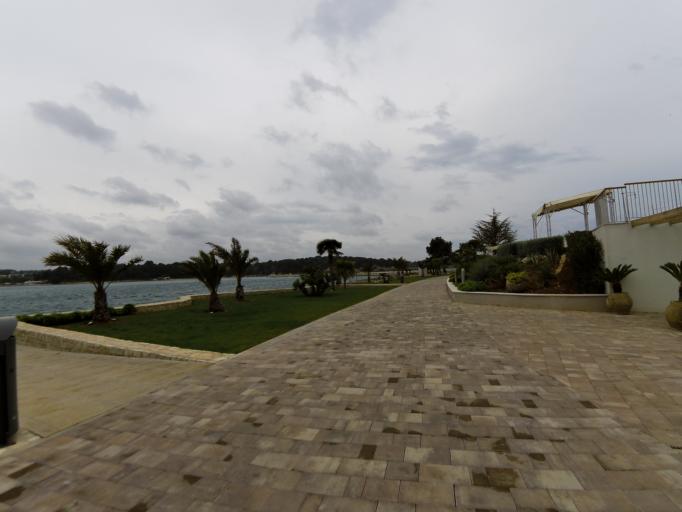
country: HR
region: Istarska
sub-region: Grad Porec
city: Porec
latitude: 45.2240
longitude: 13.5874
